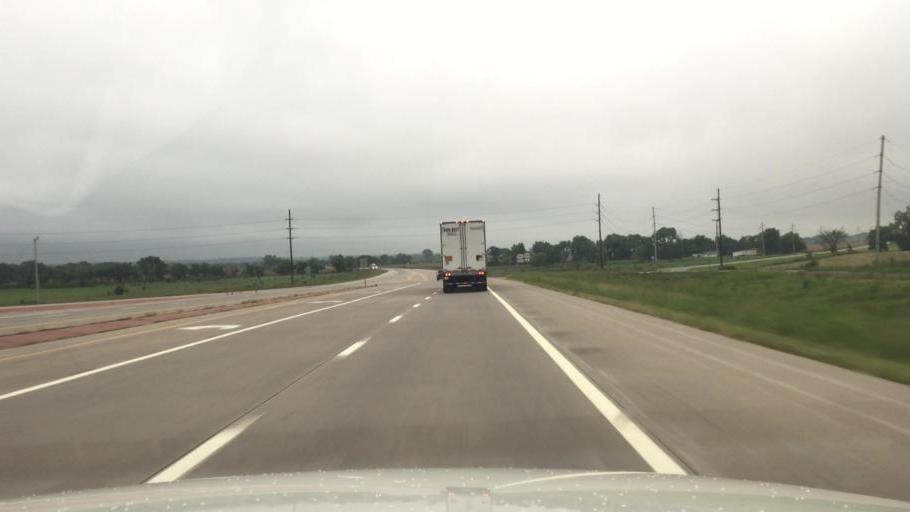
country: US
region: Kansas
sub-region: Montgomery County
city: Cherryvale
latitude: 37.2103
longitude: -95.5851
